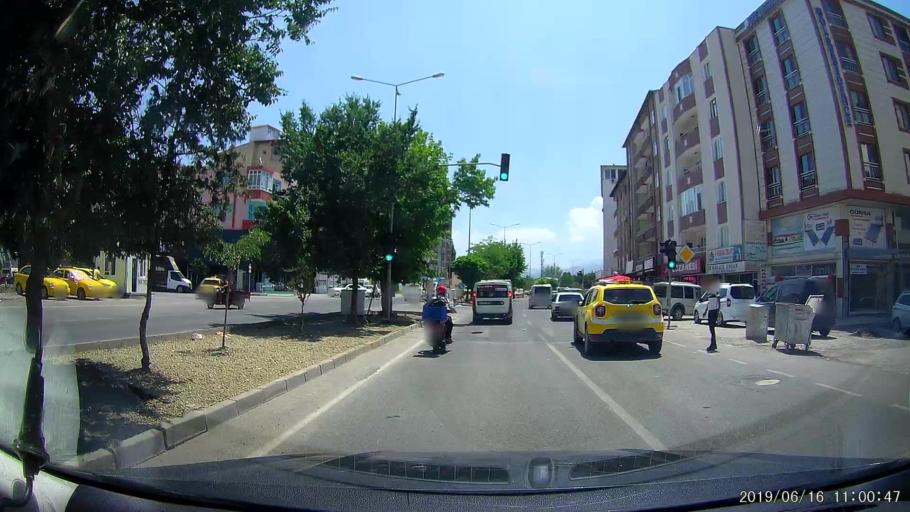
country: TR
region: Igdir
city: Igdir
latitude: 39.9178
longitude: 44.0458
